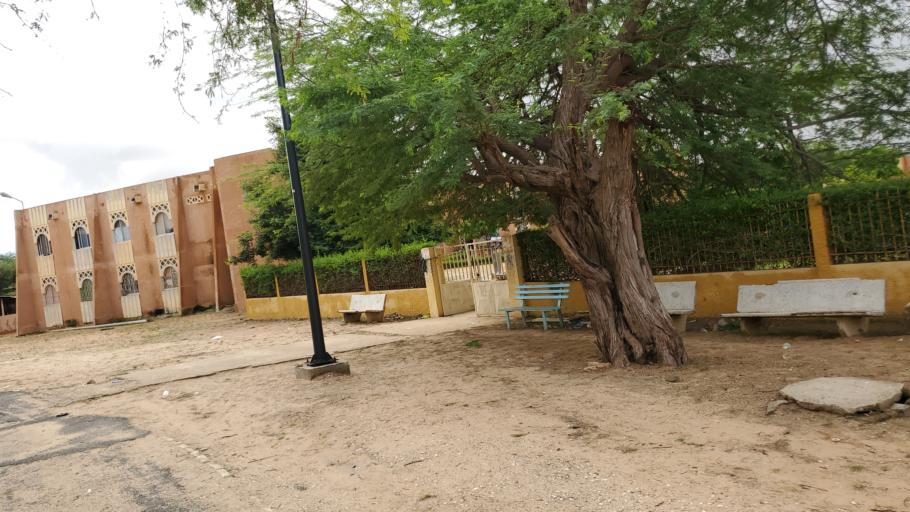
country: SN
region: Saint-Louis
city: Saint-Louis
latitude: 16.0637
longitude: -16.4269
